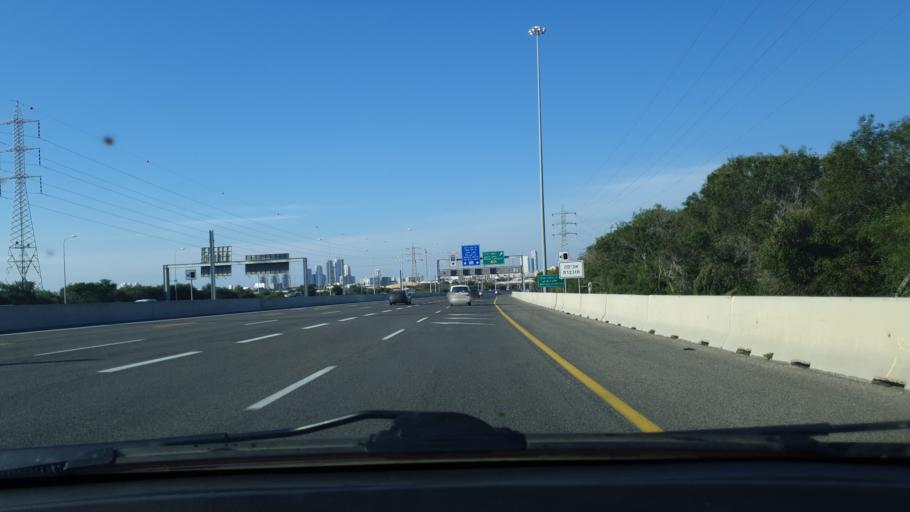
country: IL
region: Central District
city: Rishon LeZiyyon
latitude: 31.9740
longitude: 34.7564
